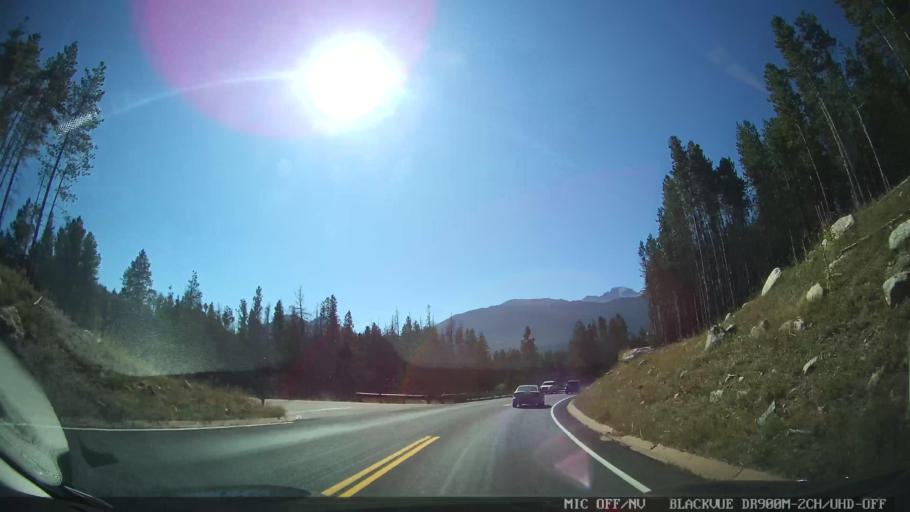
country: US
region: Colorado
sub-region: Larimer County
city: Estes Park
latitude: 40.3344
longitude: -105.5989
